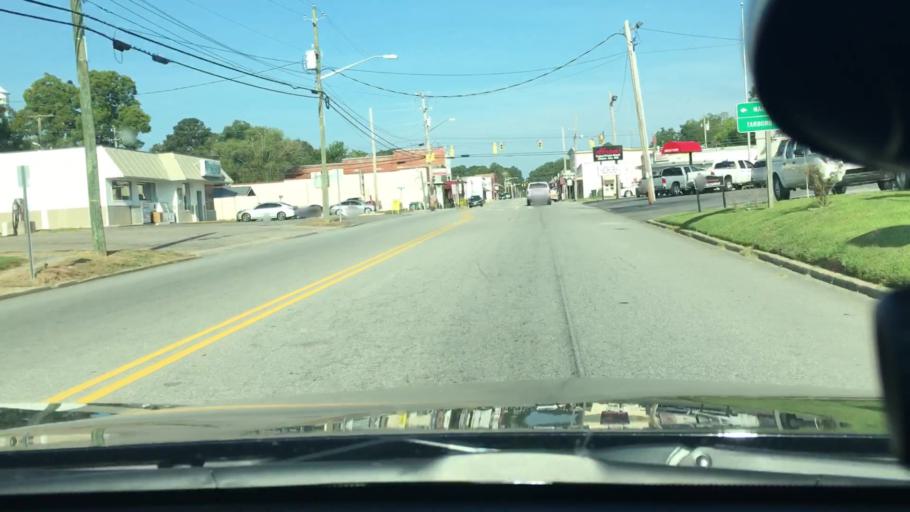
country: US
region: North Carolina
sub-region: Edgecombe County
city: Pinetops
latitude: 35.7904
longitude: -77.6356
